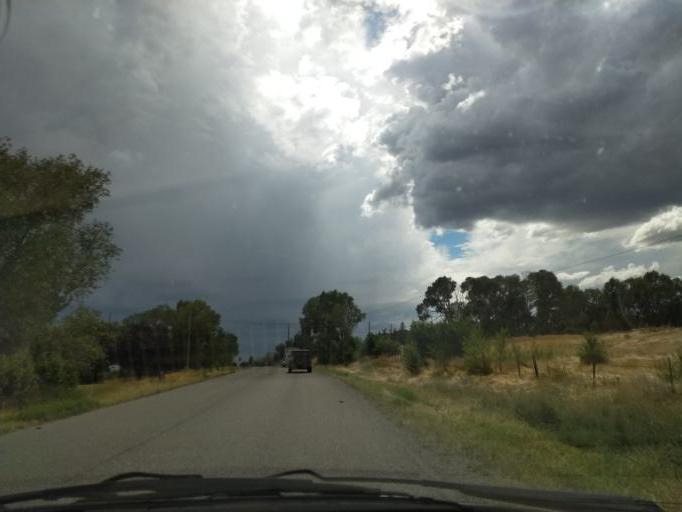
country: US
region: Colorado
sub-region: Delta County
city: Paonia
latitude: 38.8900
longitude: -107.5827
